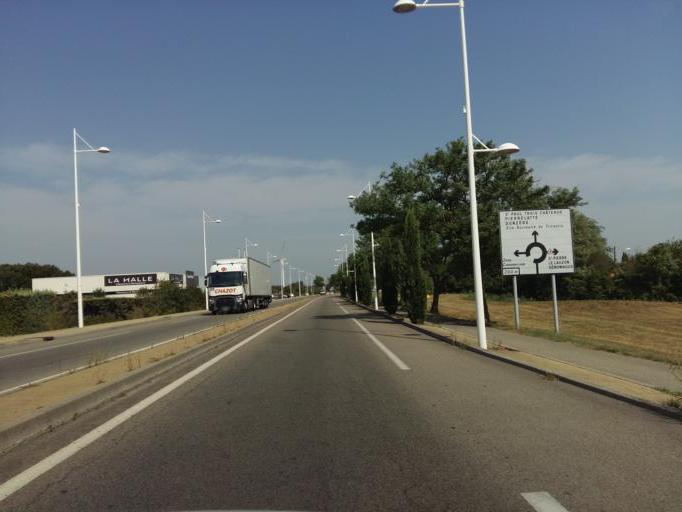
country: FR
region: Provence-Alpes-Cote d'Azur
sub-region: Departement du Vaucluse
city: Bollene
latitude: 44.2993
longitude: 4.7495
